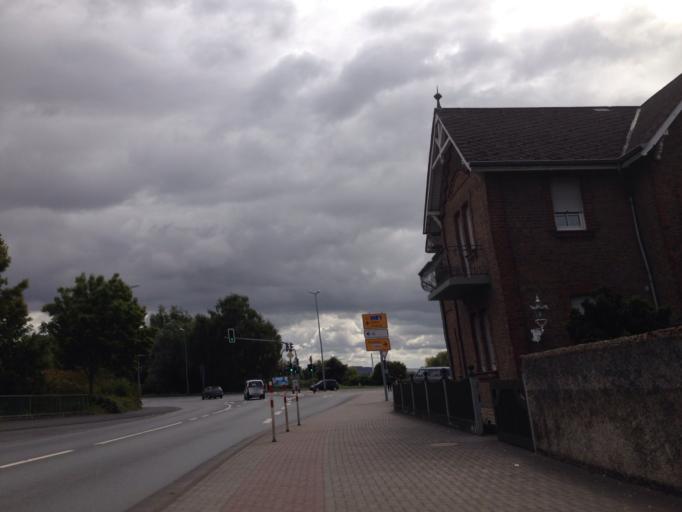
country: DE
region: Hesse
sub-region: Regierungsbezirk Giessen
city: Limburg an der Lahn
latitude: 50.4001
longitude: 8.0476
